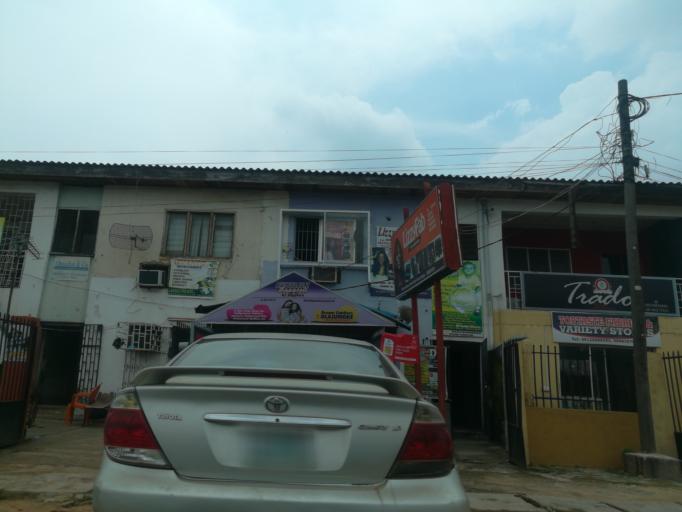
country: NG
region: Oyo
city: Ibadan
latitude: 7.4230
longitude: 3.9129
